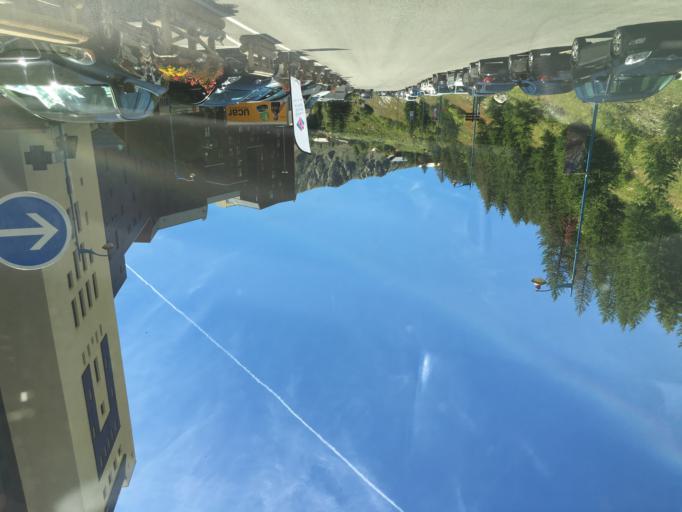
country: IT
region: Piedmont
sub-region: Provincia di Cuneo
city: Vinadio
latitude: 44.1853
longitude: 7.1601
